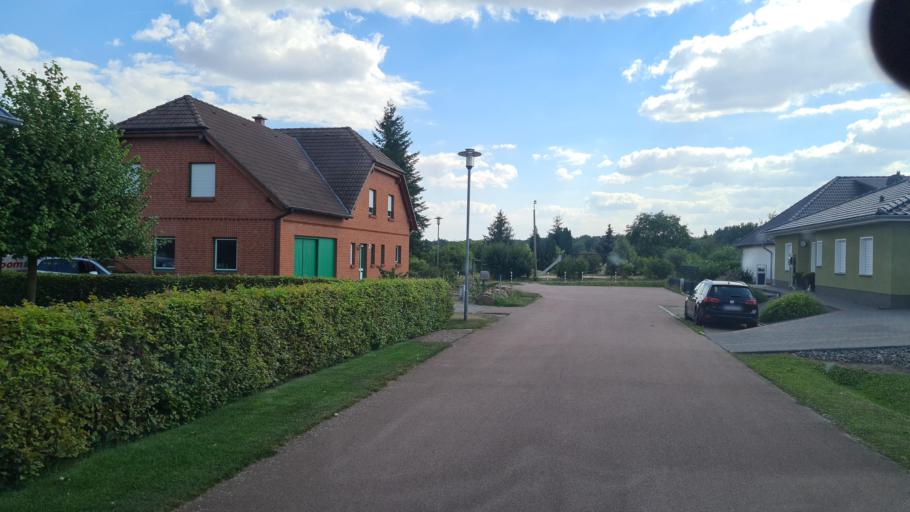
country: DE
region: Saxony-Anhalt
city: Zahna
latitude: 51.9117
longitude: 12.7818
